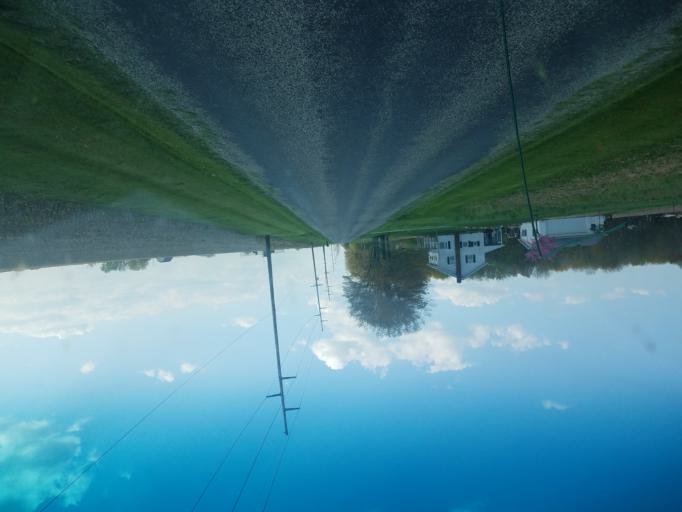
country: US
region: Ohio
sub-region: Wayne County
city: Smithville
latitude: 40.8380
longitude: -81.8777
